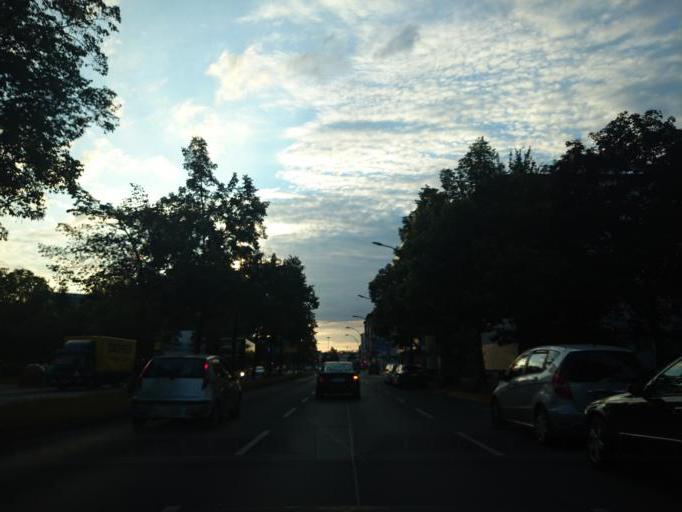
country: DE
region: Berlin
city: Reinickendorf
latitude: 52.5614
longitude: 13.3329
